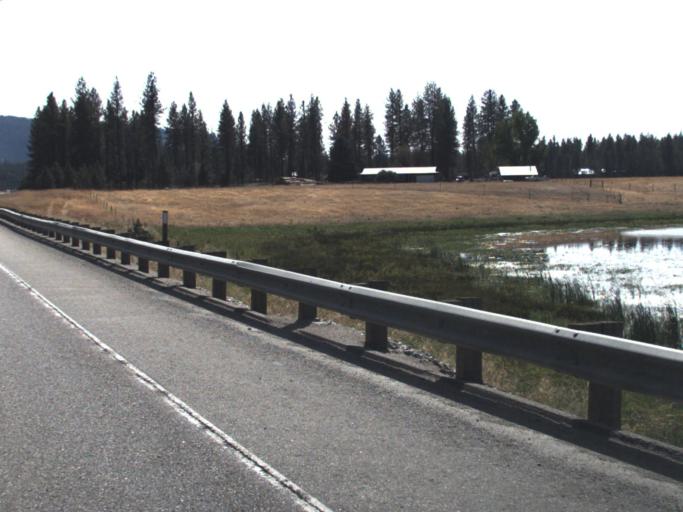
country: US
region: Washington
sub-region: Stevens County
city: Chewelah
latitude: 48.1626
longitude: -117.6958
